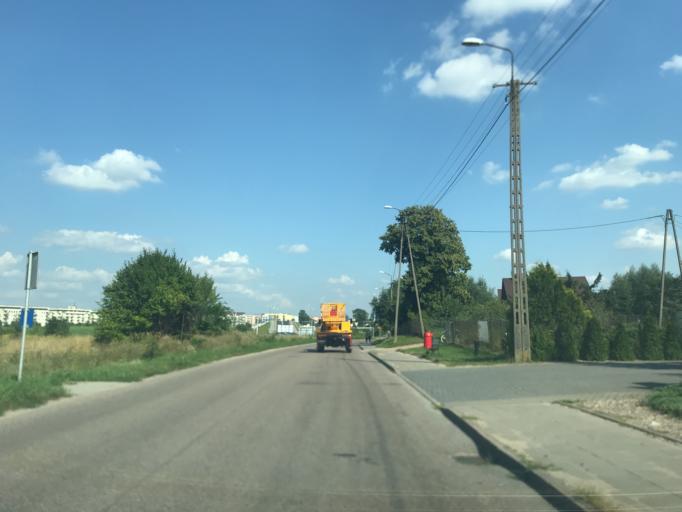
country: PL
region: Masovian Voivodeship
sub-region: Powiat mlawski
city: Mlawa
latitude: 53.1087
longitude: 20.3578
